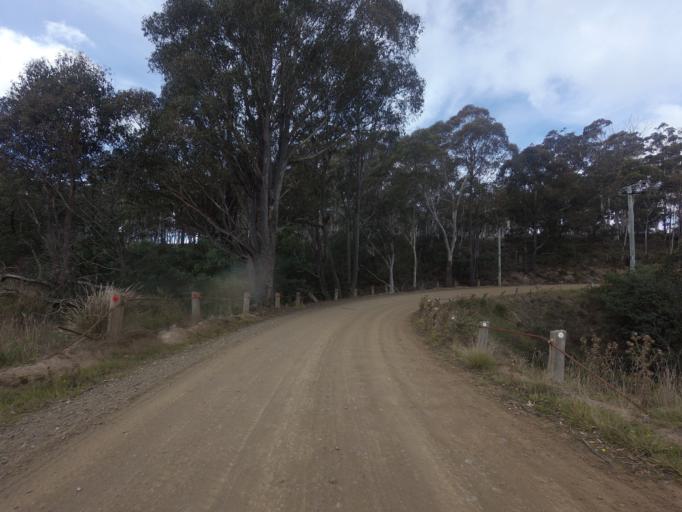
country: AU
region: Tasmania
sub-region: Brighton
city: Bridgewater
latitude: -42.4278
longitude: 147.4342
